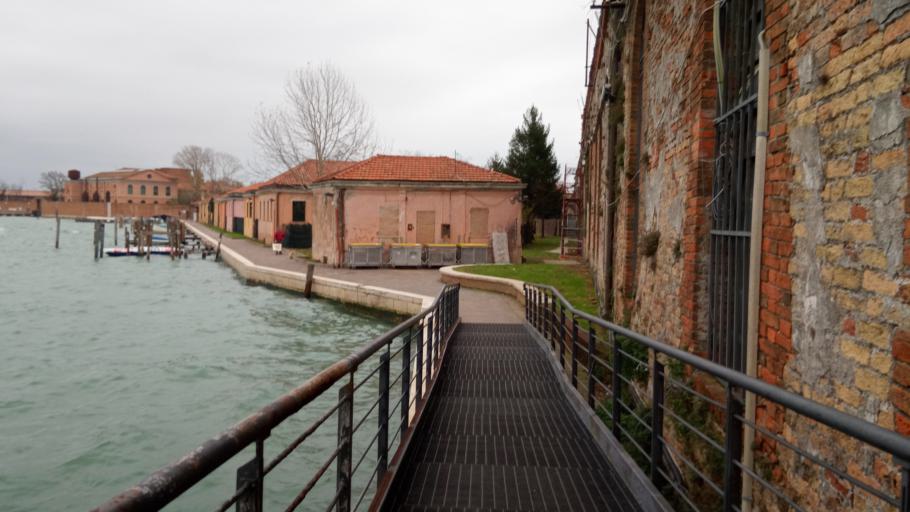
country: IT
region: Veneto
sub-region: Provincia di Venezia
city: Murano
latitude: 45.4381
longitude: 12.3541
